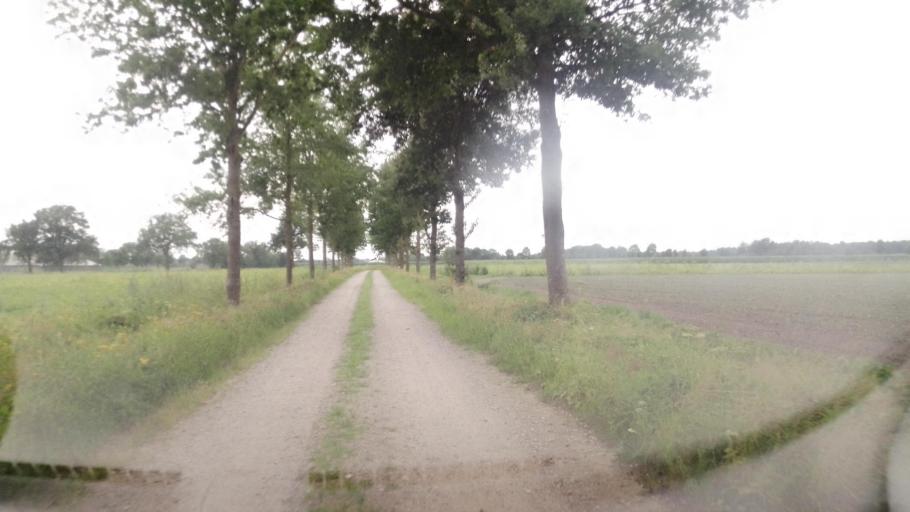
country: NL
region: Limburg
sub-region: Gemeente Peel en Maas
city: Maasbree
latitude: 51.3899
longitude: 6.0149
